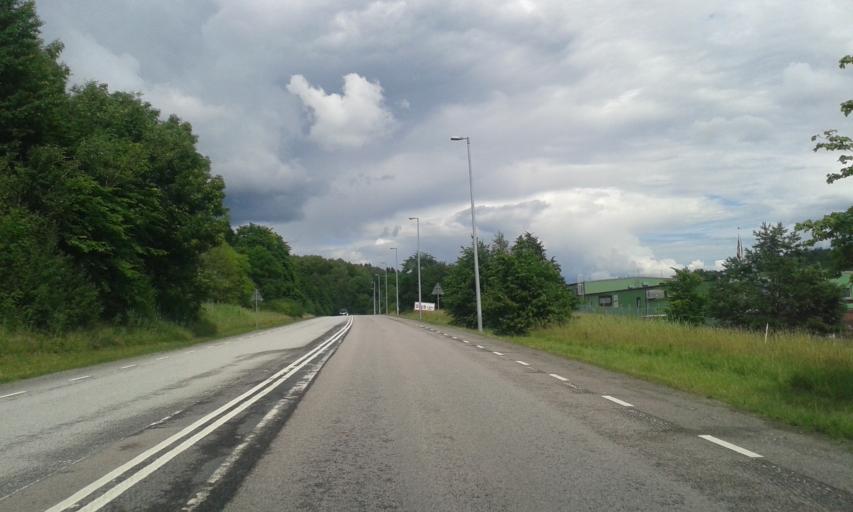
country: SE
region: Vaestra Goetaland
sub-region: Kungalvs Kommun
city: Kungalv
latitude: 57.8825
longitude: 11.9814
